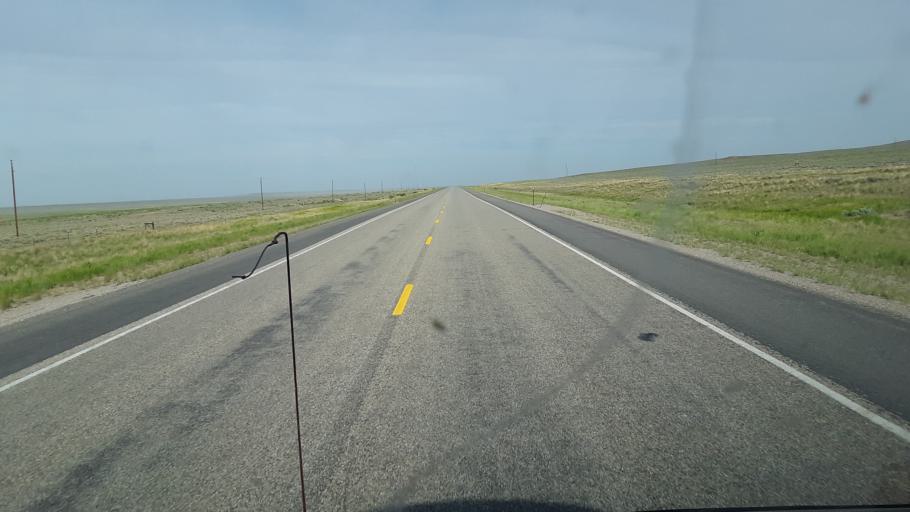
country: US
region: Wyoming
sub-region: Fremont County
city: Riverton
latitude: 43.1399
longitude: -107.5898
